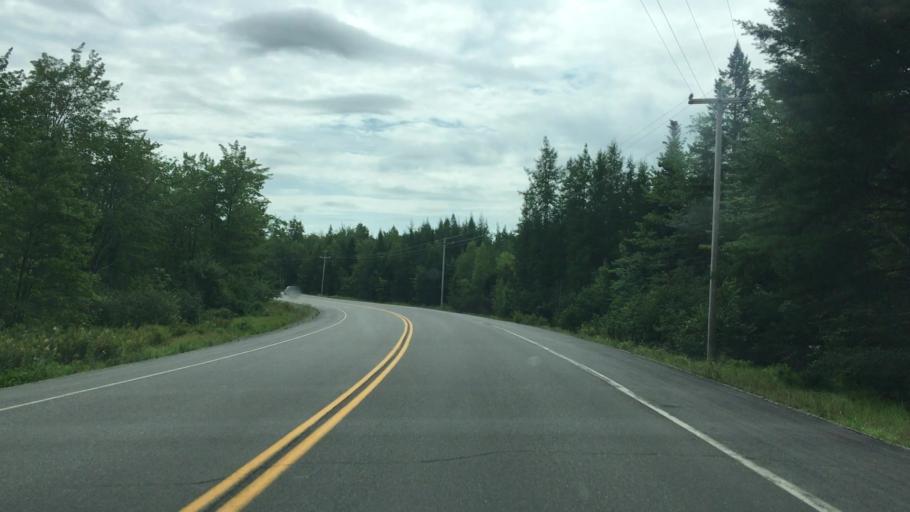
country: US
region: Maine
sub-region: Washington County
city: Machias
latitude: 44.9993
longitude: -67.5689
